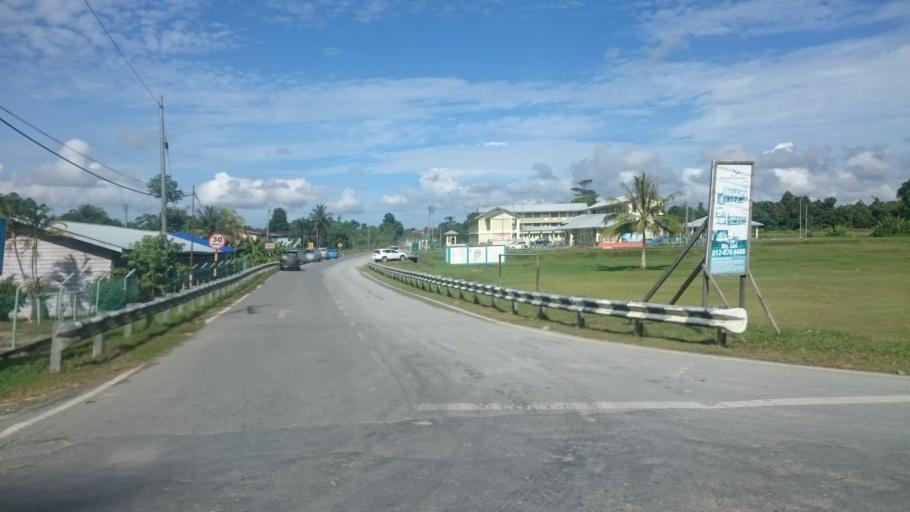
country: MY
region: Sarawak
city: Limbang
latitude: 4.7240
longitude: 114.9915
